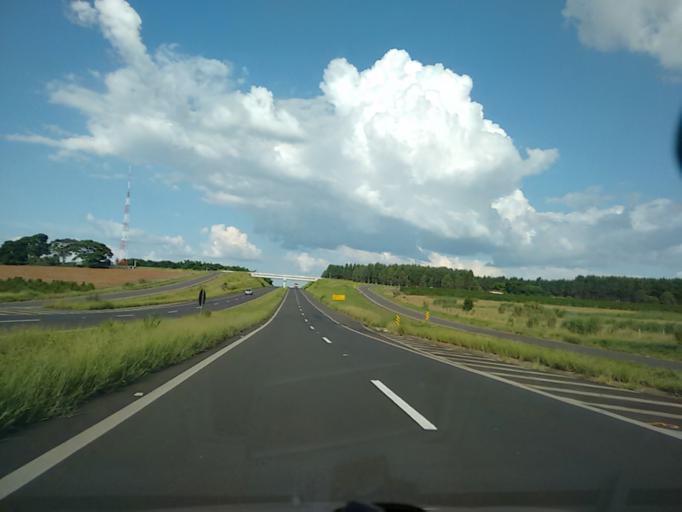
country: BR
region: Sao Paulo
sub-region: Duartina
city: Duartina
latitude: -22.3305
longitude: -49.4548
